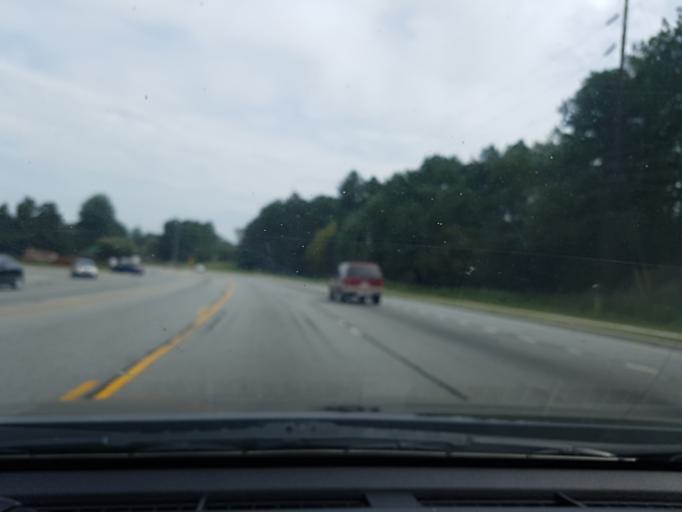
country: US
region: Georgia
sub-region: Gwinnett County
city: Lilburn
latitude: 33.9343
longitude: -84.1573
